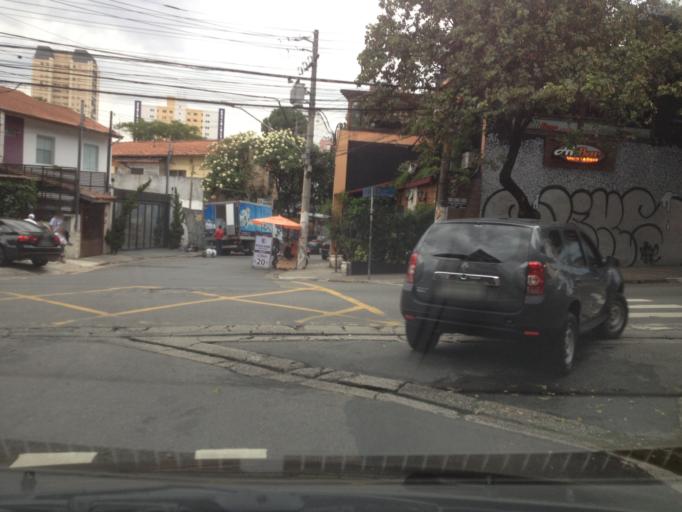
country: BR
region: Sao Paulo
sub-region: Sao Paulo
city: Sao Paulo
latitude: -23.5590
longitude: -46.6880
